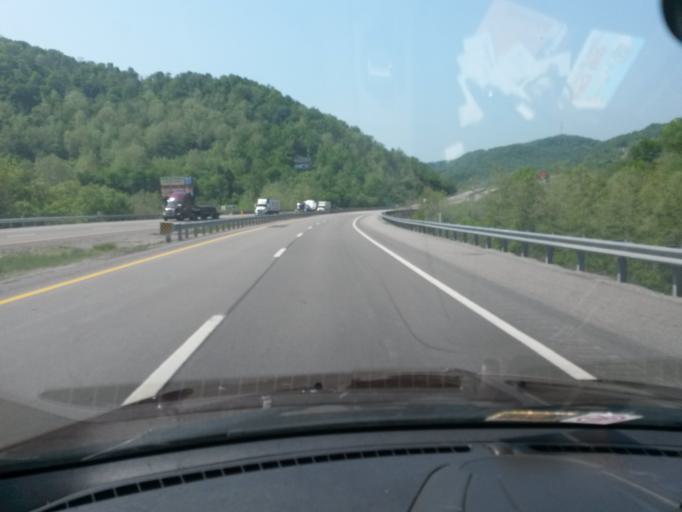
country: US
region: West Virginia
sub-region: Gilmer County
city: Glenville
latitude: 38.8657
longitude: -80.6487
